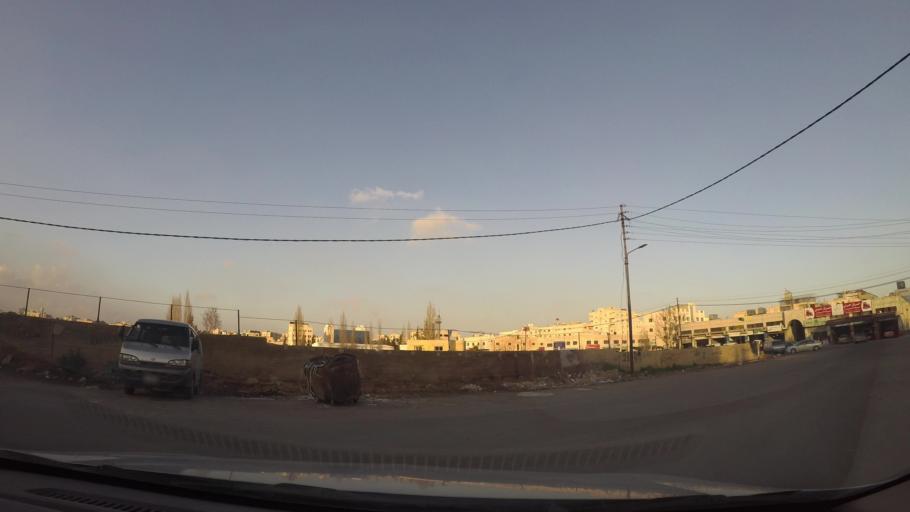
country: JO
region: Amman
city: Al Bunayyat ash Shamaliyah
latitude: 31.9102
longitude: 35.9192
